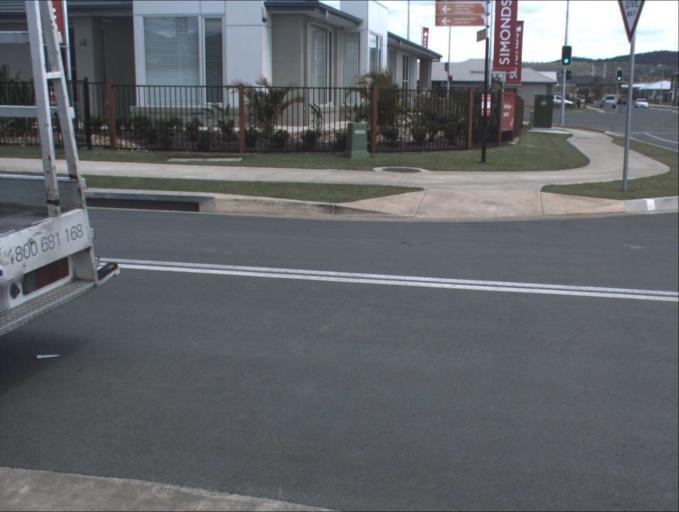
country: AU
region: Queensland
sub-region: Logan
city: Chambers Flat
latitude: -27.8055
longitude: 153.1140
